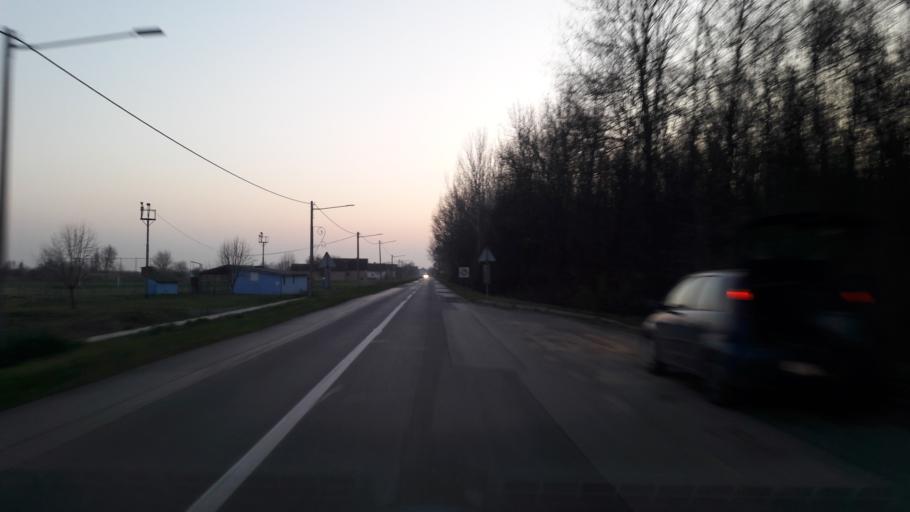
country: HR
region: Vukovarsko-Srijemska
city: Nijemci
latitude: 45.1920
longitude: 19.0186
